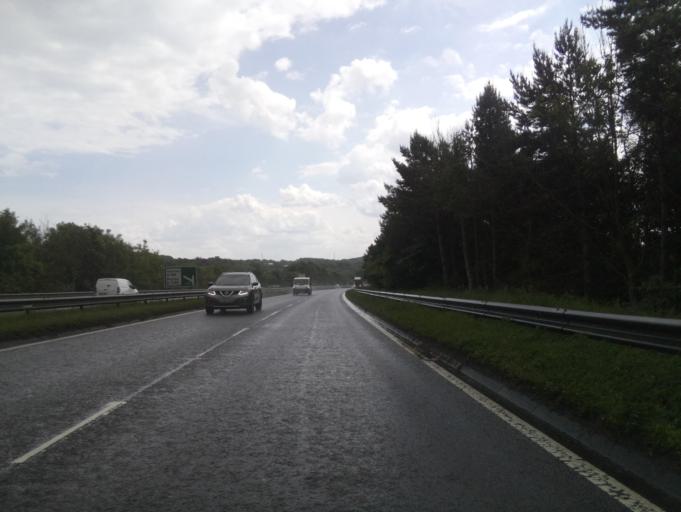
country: GB
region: England
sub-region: County Durham
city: Seaham
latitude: 54.8250
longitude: -1.3701
